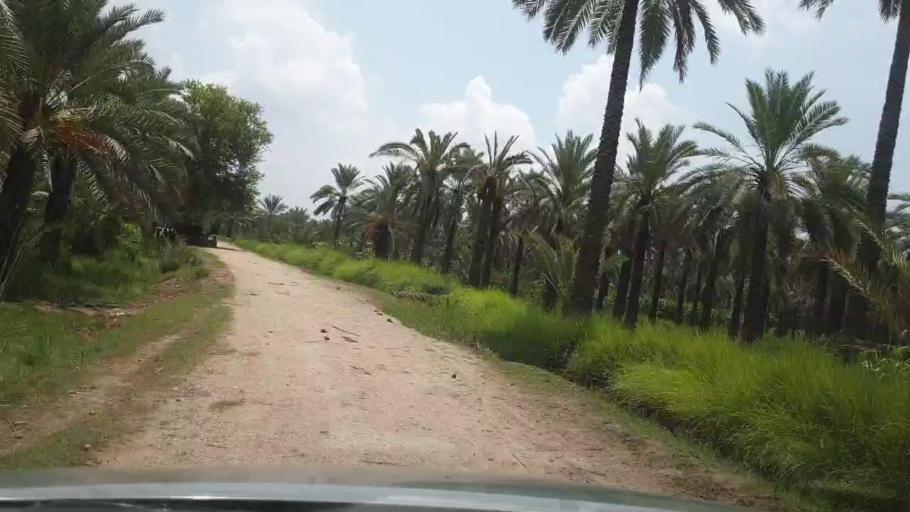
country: PK
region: Sindh
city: Khairpur
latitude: 27.6282
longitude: 68.7398
